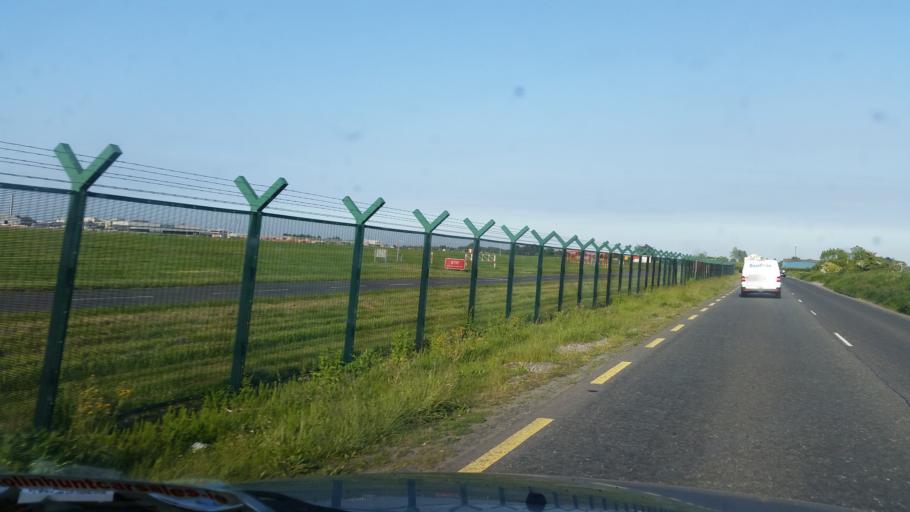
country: IE
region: Leinster
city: Ballymun
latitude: 53.4183
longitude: -6.2511
